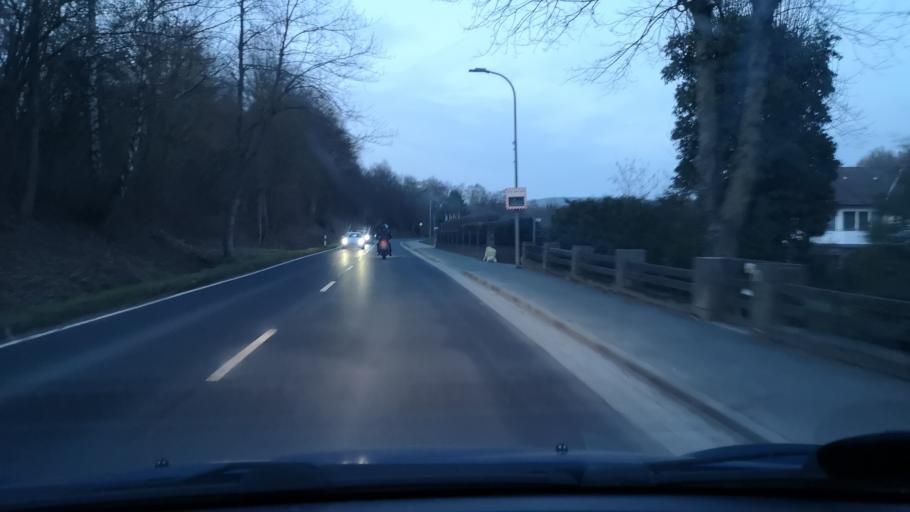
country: DE
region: Lower Saxony
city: Salzhemmendorf
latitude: 52.0695
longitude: 9.5852
